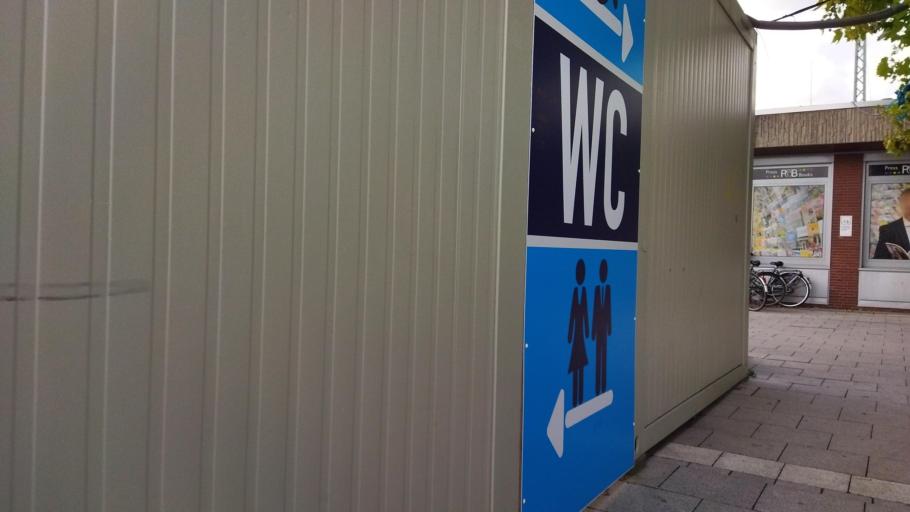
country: DE
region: Lower Saxony
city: Emden
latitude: 53.3689
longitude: 7.1961
